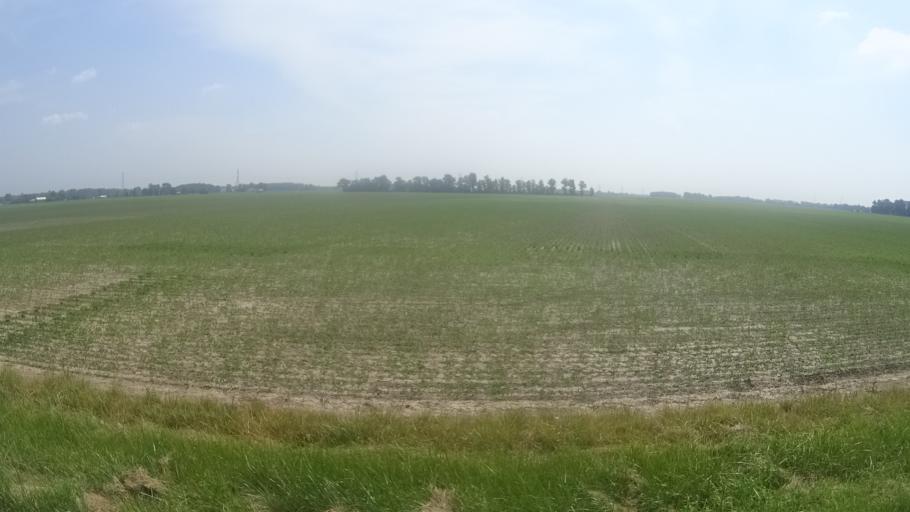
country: US
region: Ohio
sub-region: Erie County
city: Sandusky
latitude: 41.3472
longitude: -82.7253
